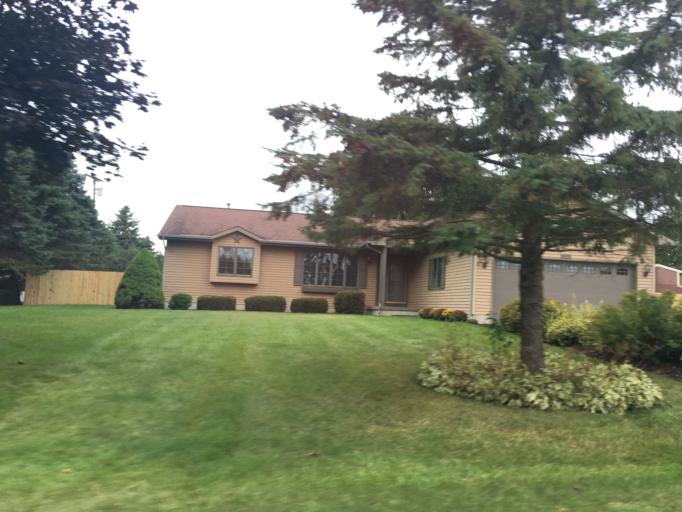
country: US
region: Michigan
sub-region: Lapeer County
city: Barnes Lake-Millers Lake
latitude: 43.3361
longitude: -83.3441
